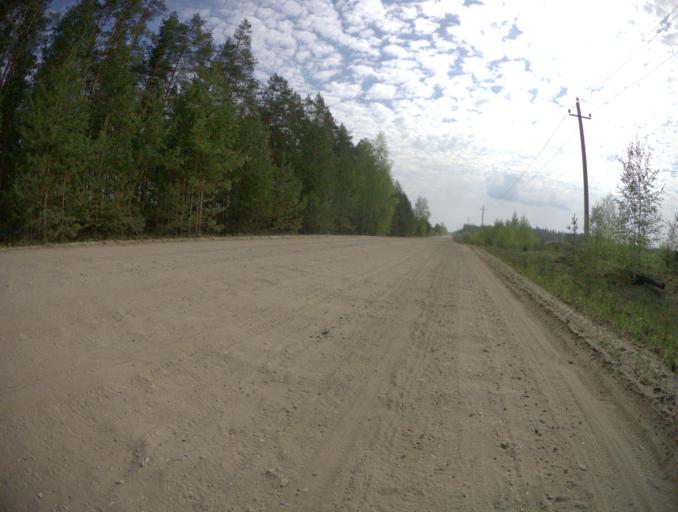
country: RU
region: Ivanovo
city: Yuzha
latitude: 56.5212
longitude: 42.0641
